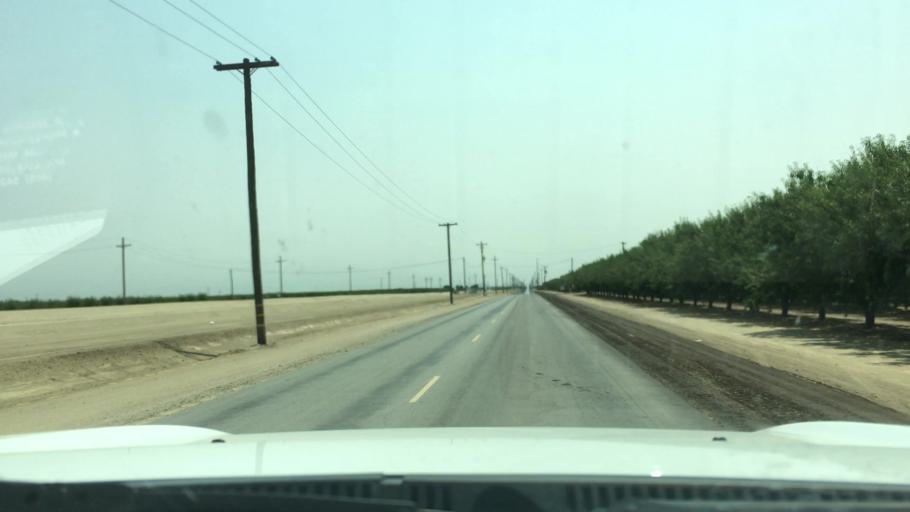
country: US
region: California
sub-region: Kern County
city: Wasco
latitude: 35.6215
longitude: -119.4379
